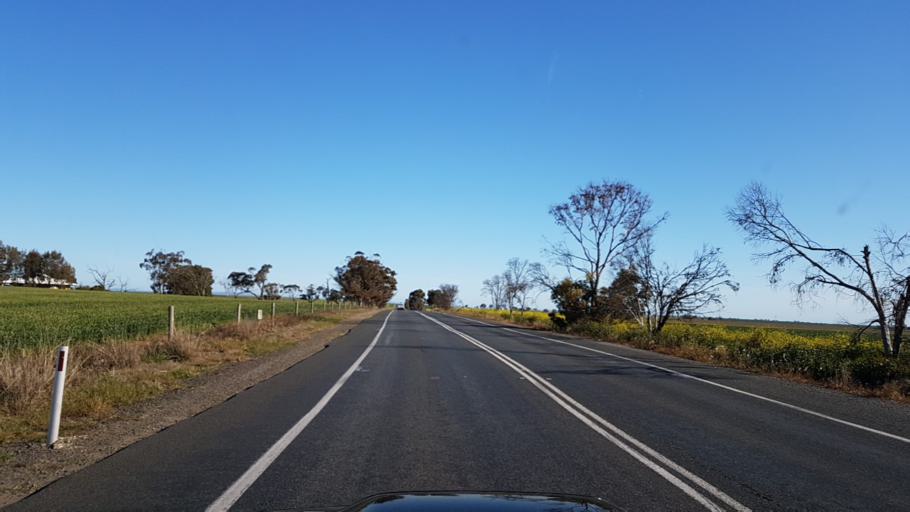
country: AU
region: South Australia
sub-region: Light
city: Freeling
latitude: -34.4064
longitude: 138.7518
